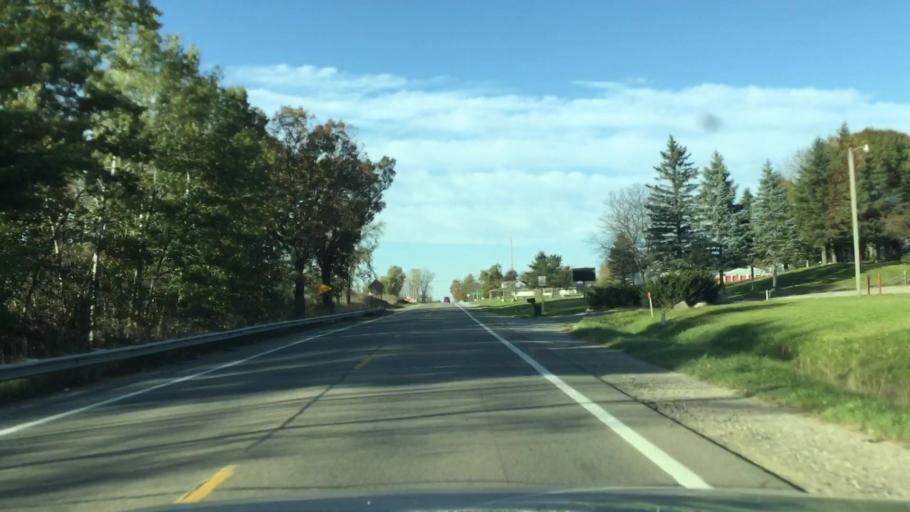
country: US
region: Michigan
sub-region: Lapeer County
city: Barnes Lake-Millers Lake
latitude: 43.1862
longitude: -83.3125
